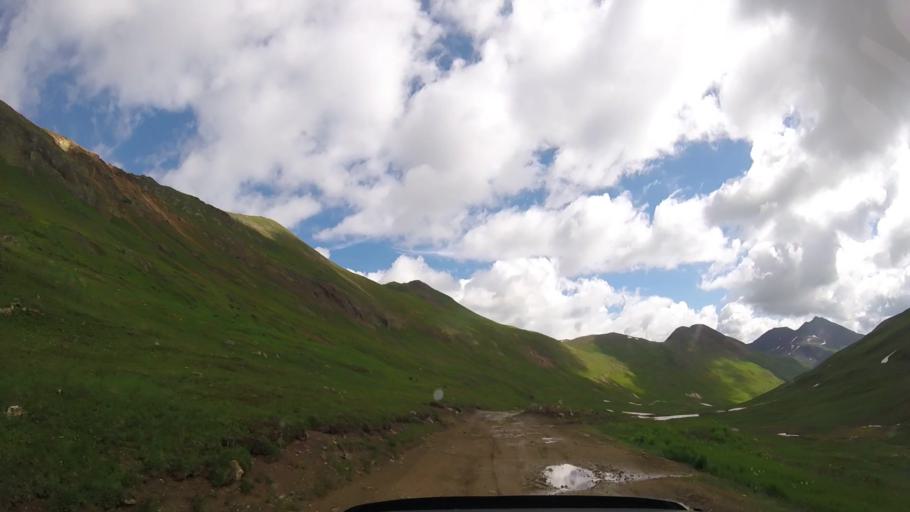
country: US
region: Colorado
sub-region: Ouray County
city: Ouray
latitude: 37.9239
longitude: -107.6114
